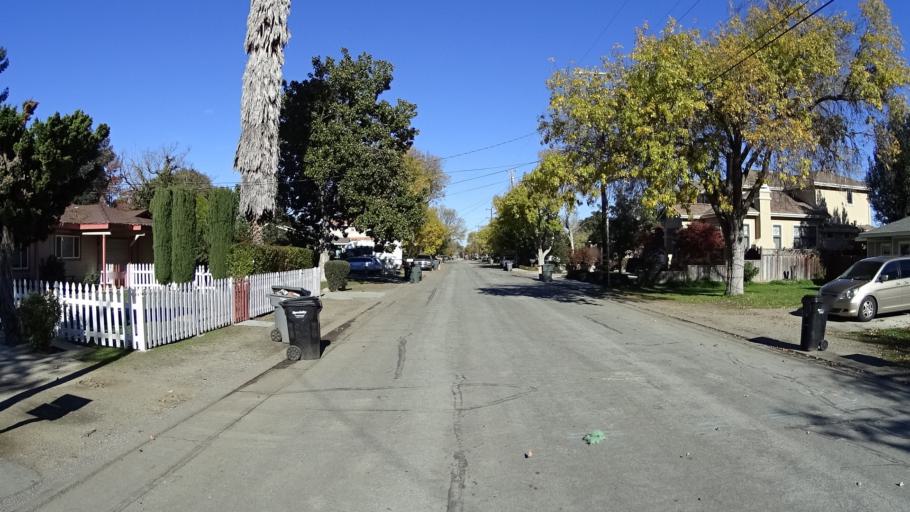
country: US
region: California
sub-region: Santa Clara County
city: Cupertino
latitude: 37.3467
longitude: -122.0111
